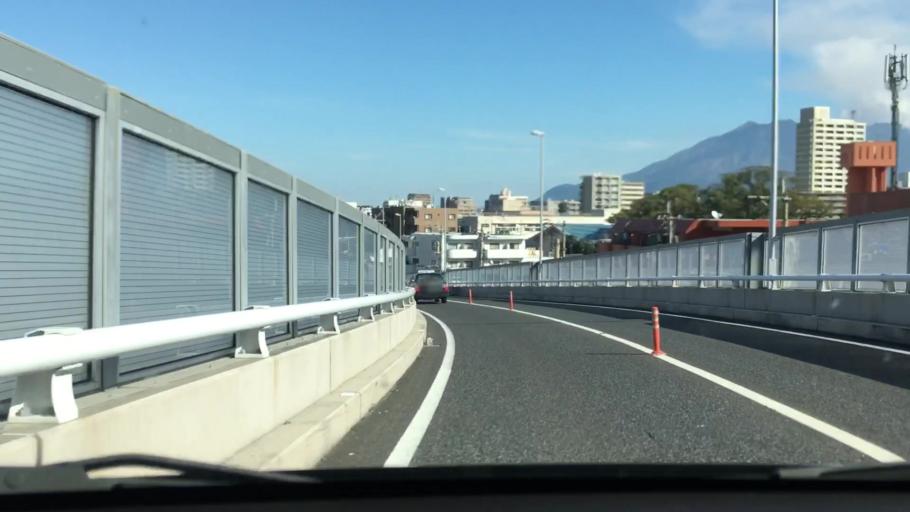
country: JP
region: Kagoshima
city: Kagoshima-shi
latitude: 31.5625
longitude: 130.5438
